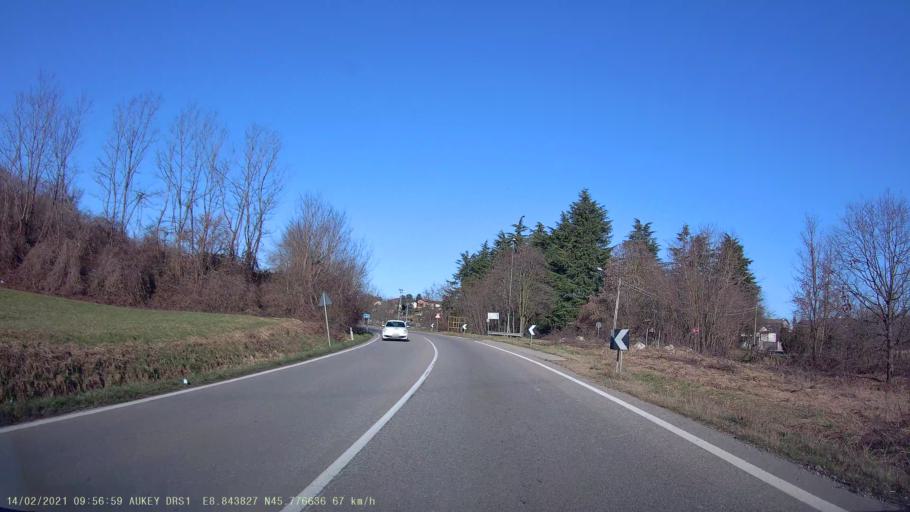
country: IT
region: Lombardy
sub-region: Provincia di Varese
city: Gazzada Schianno
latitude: 45.7769
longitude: 8.8431
